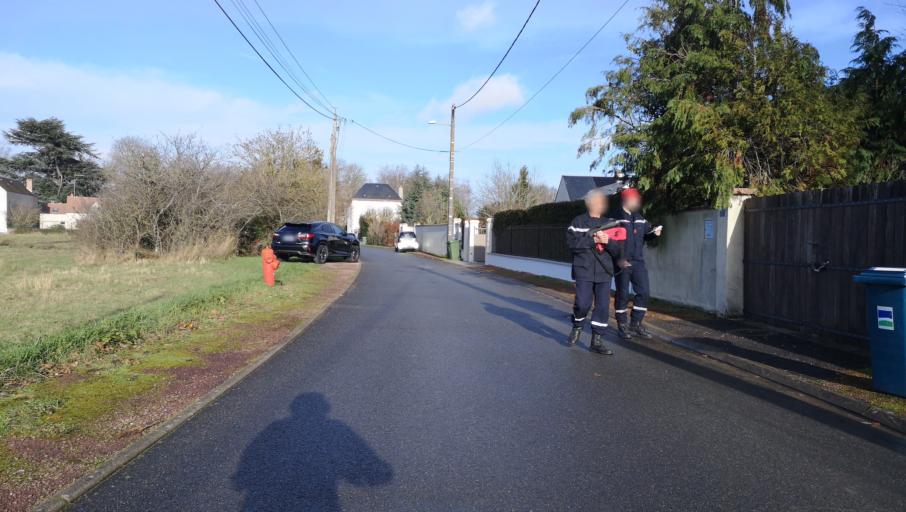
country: FR
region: Centre
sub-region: Departement du Loiret
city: Saint-Pryve-Saint-Mesmin
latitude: 47.8752
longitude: 1.8543
